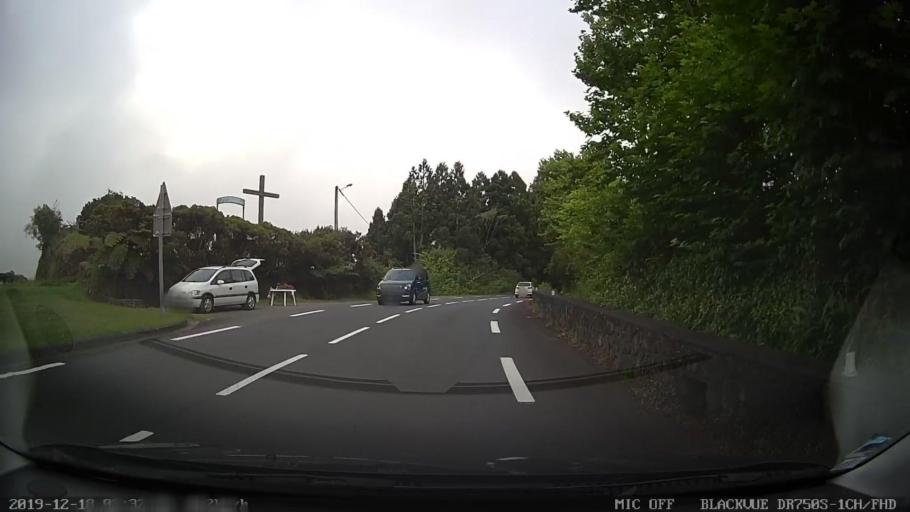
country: RE
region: Reunion
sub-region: Reunion
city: Cilaos
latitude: -21.1527
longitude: 55.6114
